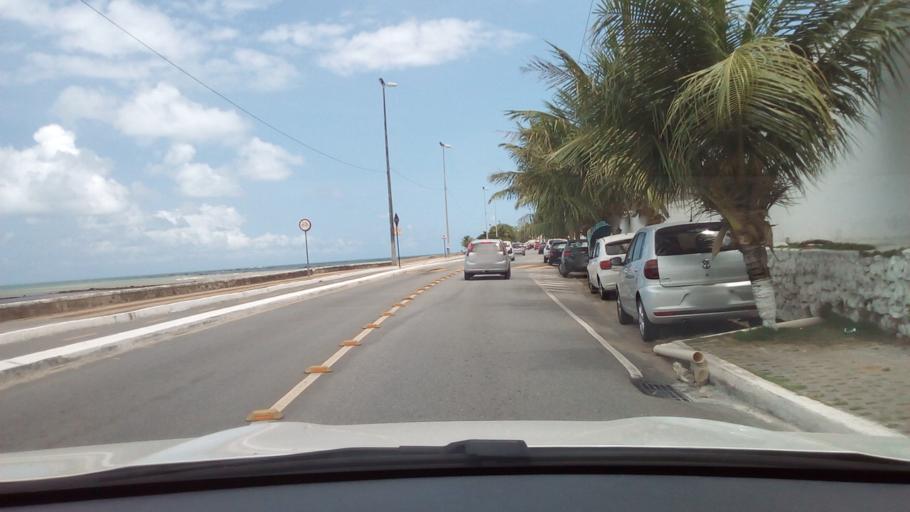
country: BR
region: Paraiba
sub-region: Joao Pessoa
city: Joao Pessoa
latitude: -7.1456
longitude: -34.8065
